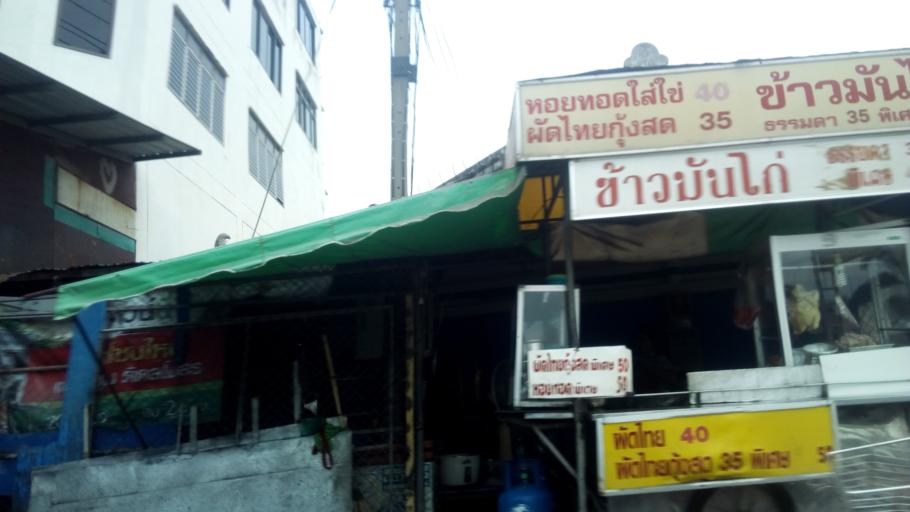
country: TH
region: Nakhon Pathom
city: Salaya
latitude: 13.7680
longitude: 100.2860
